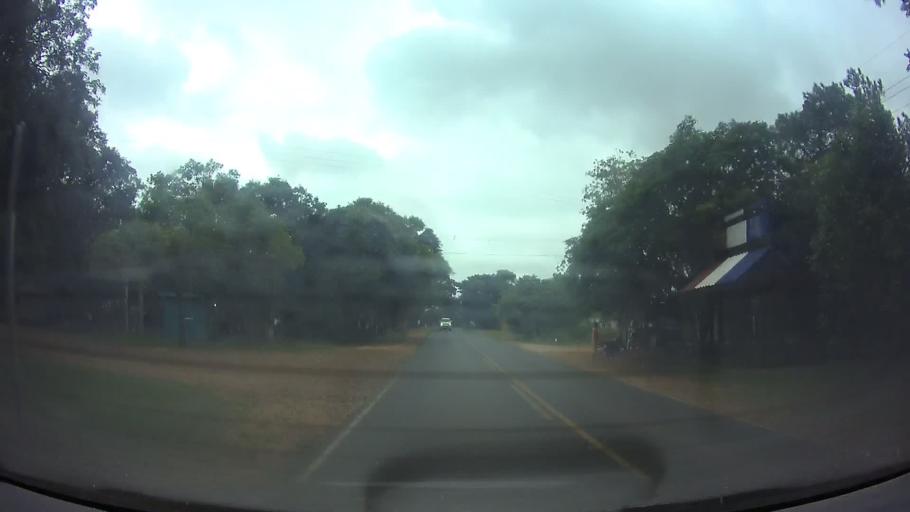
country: PY
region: Central
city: Guarambare
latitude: -25.5331
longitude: -57.4997
